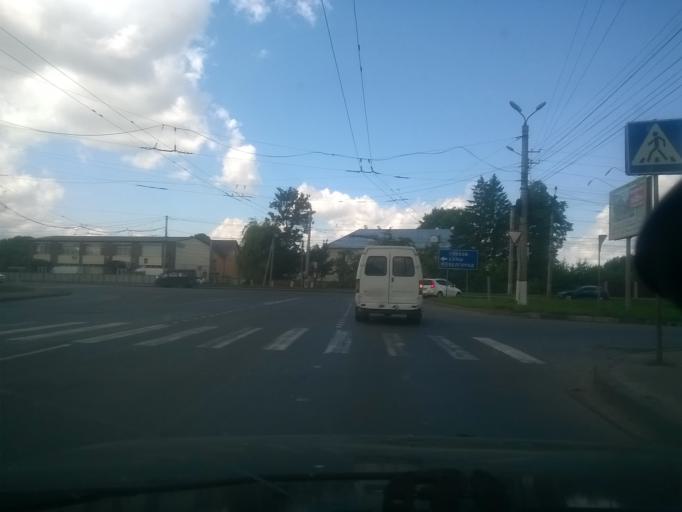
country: RU
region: Kursk
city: Kursk
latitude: 51.6504
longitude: 36.1303
